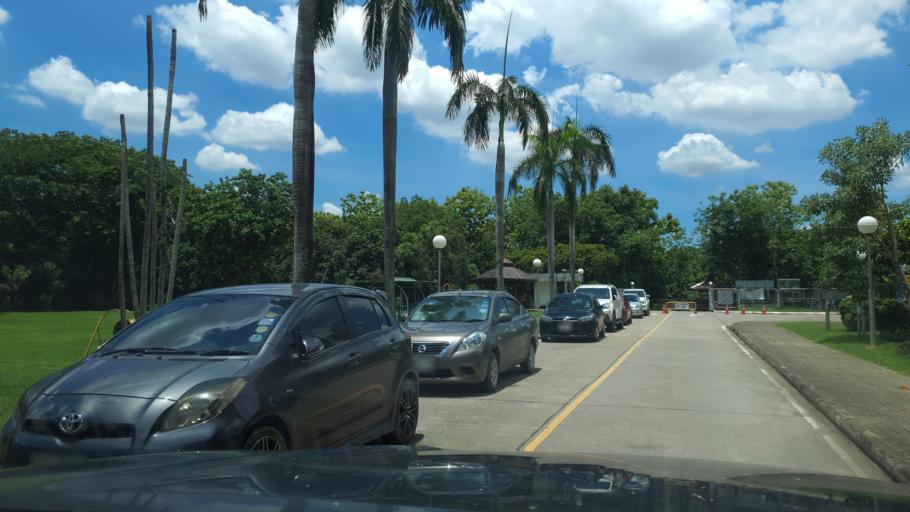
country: TH
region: Chiang Mai
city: Chiang Mai
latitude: 18.8507
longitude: 98.9632
